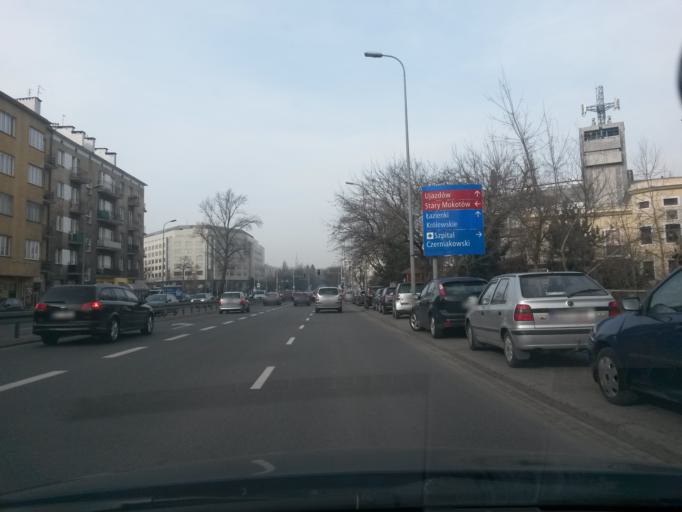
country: PL
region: Masovian Voivodeship
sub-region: Warszawa
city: Mokotow
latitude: 52.2056
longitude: 21.0321
